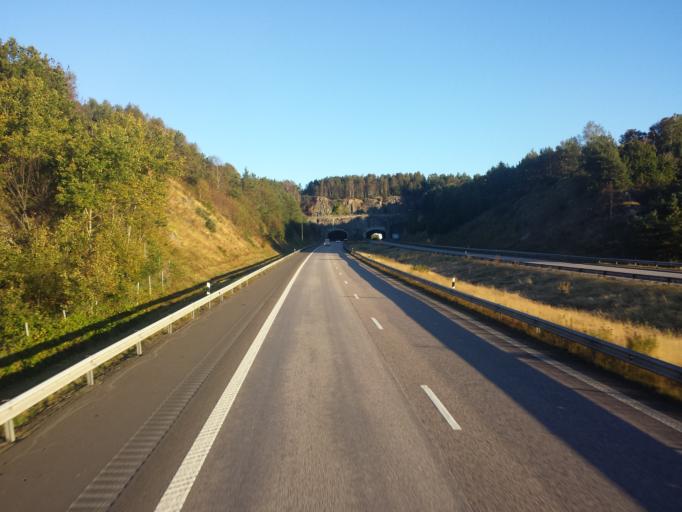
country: SE
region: Halland
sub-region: Varbergs Kommun
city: Veddige
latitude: 57.2318
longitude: 12.2258
